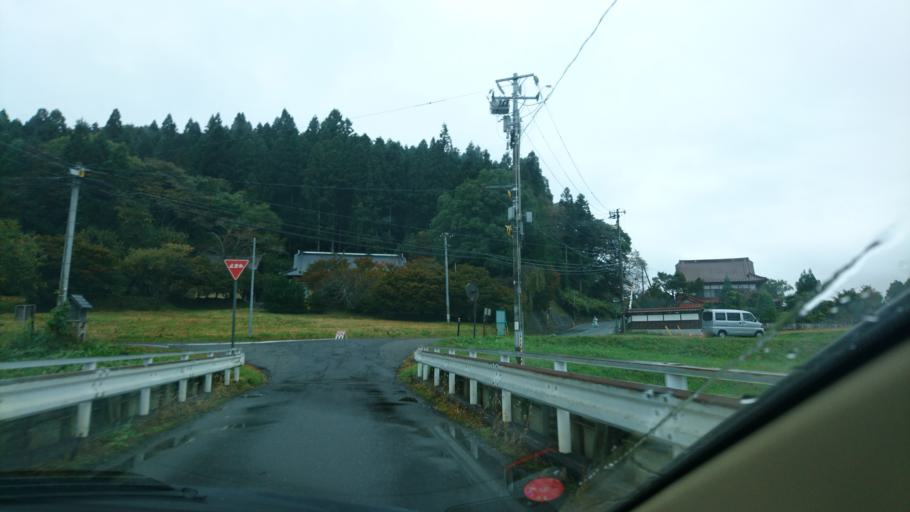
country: JP
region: Iwate
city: Ichinoseki
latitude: 38.9775
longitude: 141.1029
